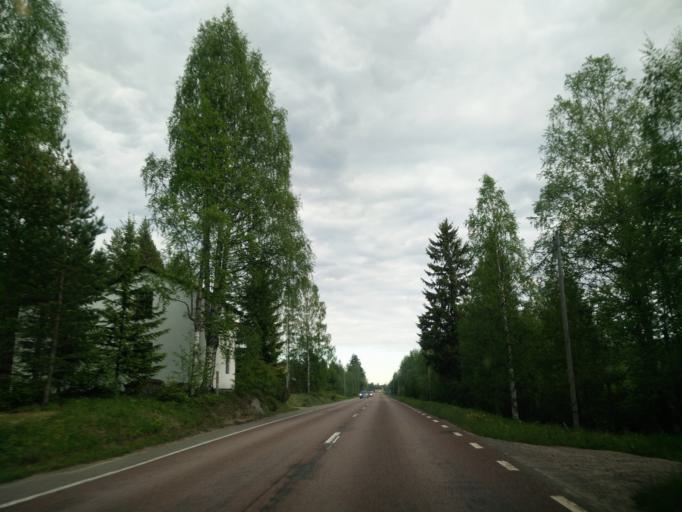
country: SE
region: Jaemtland
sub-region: Harjedalens Kommun
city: Sveg
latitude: 62.2905
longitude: 14.7928
